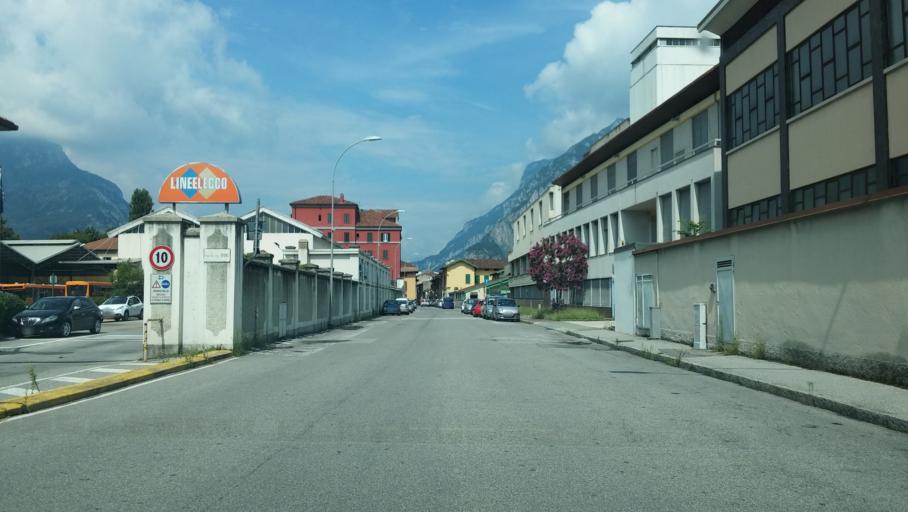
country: IT
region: Lombardy
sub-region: Provincia di Lecco
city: Pescate
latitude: 45.8423
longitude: 9.4006
